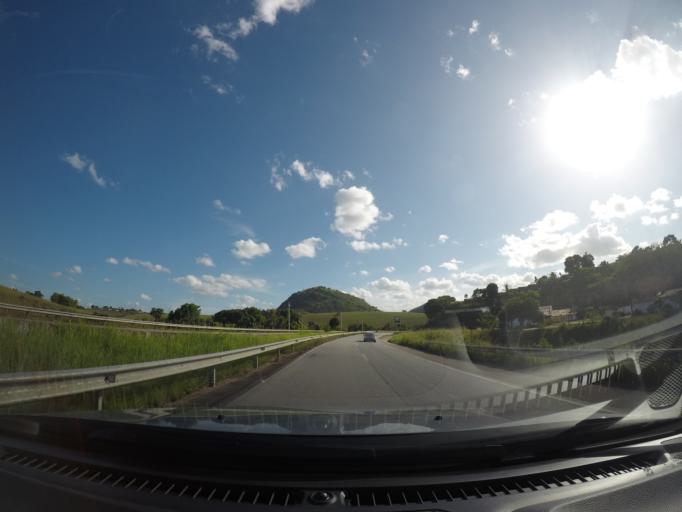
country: BR
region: Alagoas
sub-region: Flexeiras
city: Flexeiras
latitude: -9.1178
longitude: -35.7648
